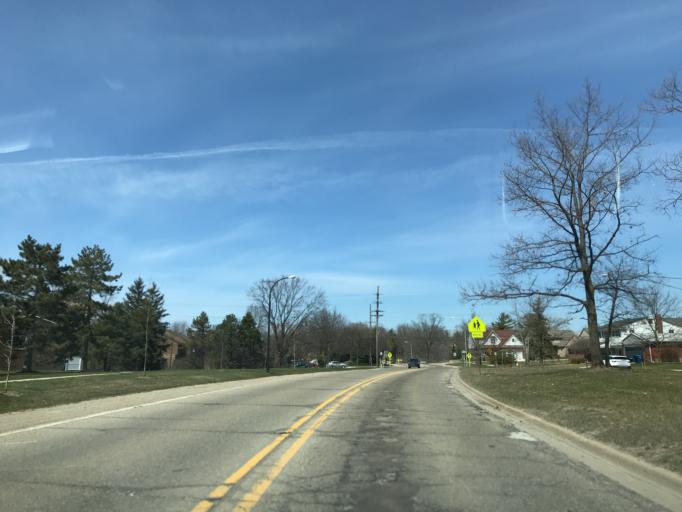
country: US
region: Michigan
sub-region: Washtenaw County
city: Ann Arbor
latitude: 42.3086
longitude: -83.7077
